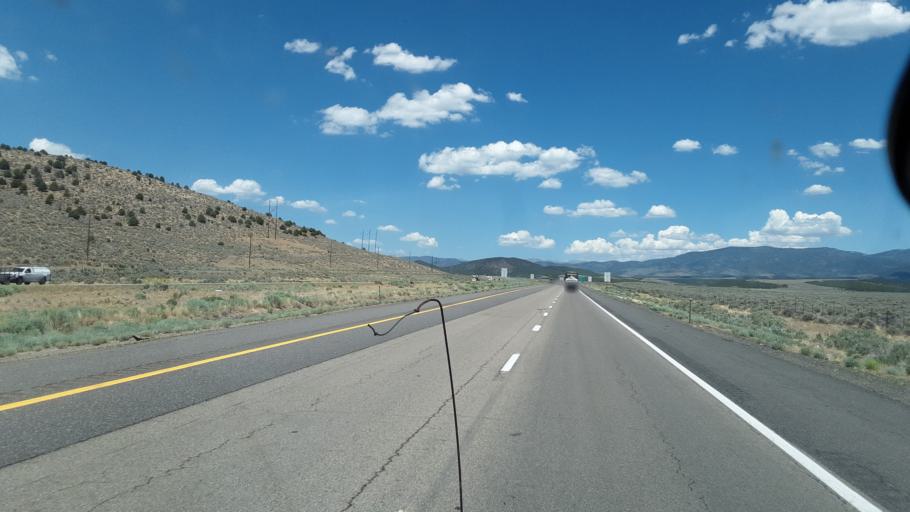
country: US
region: Utah
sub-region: Beaver County
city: Beaver
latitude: 38.1106
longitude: -112.6456
